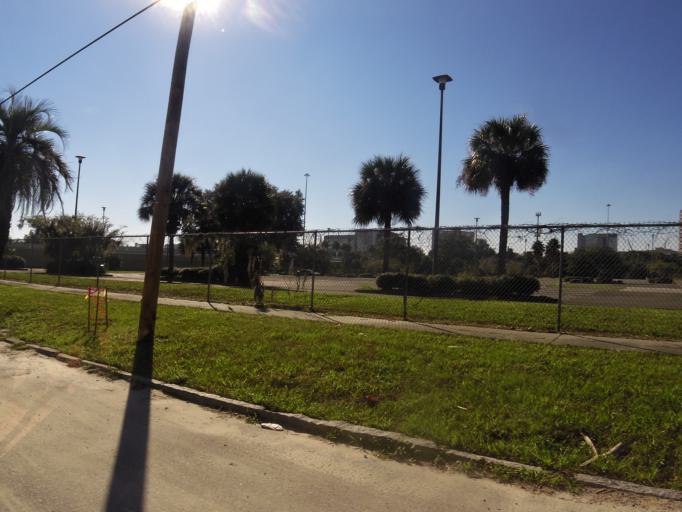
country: US
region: Florida
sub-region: Duval County
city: Jacksonville
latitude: 30.3154
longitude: -81.6566
